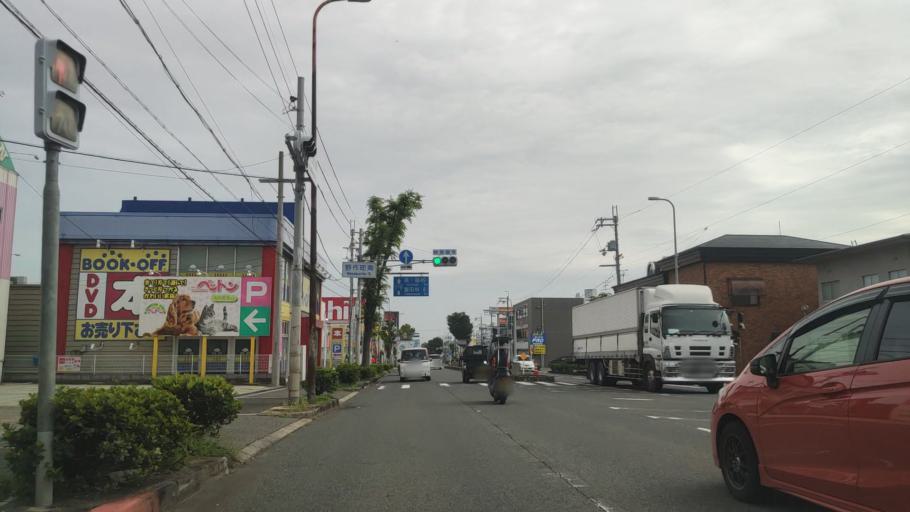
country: JP
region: Osaka
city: Tondabayashicho
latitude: 34.4498
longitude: 135.5578
